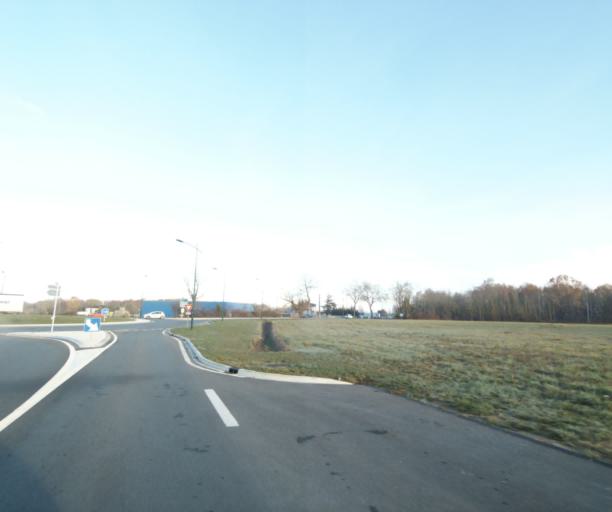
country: FR
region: Poitou-Charentes
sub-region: Departement de la Charente-Maritime
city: Fontcouverte
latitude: 45.7653
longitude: -0.5829
